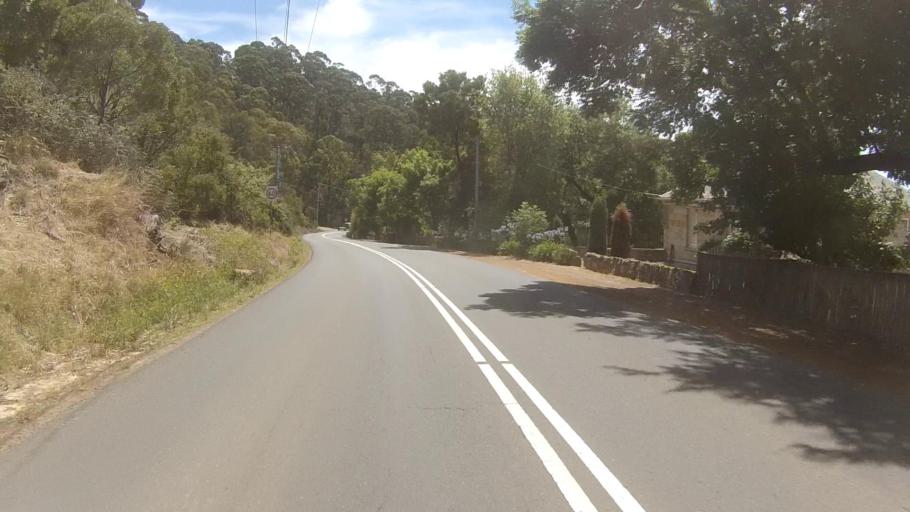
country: AU
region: Tasmania
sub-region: Kingborough
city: Kingston Beach
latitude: -42.9627
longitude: 147.3314
